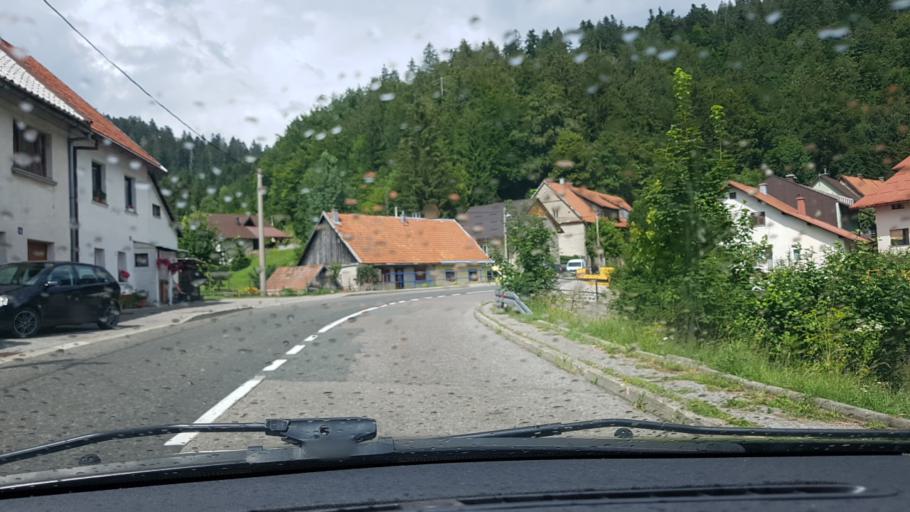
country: HR
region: Primorsko-Goranska
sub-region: Grad Delnice
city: Delnice
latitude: 45.3623
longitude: 14.7537
